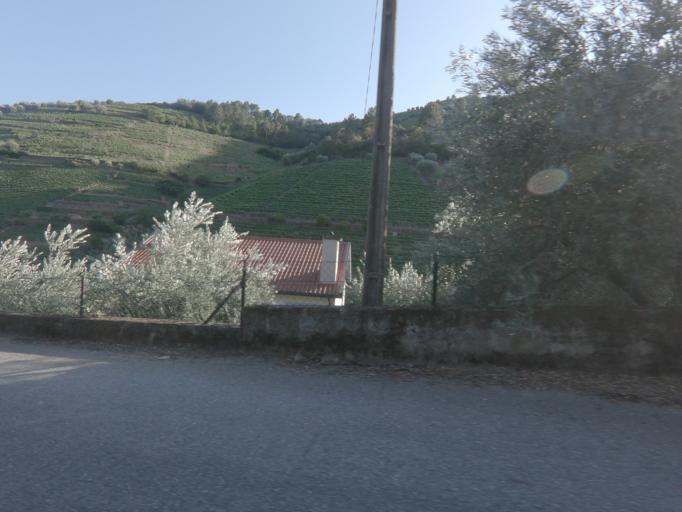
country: PT
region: Vila Real
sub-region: Sabrosa
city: Vilela
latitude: 41.1834
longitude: -7.5852
